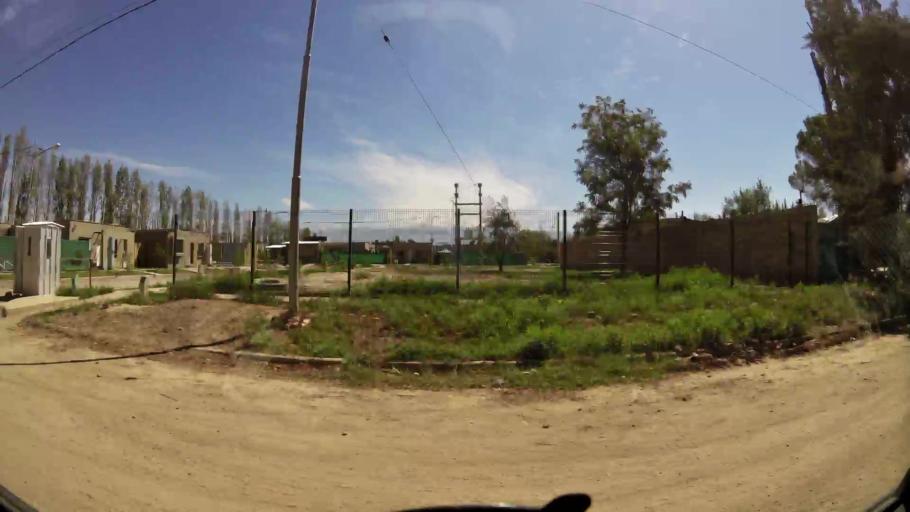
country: AR
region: Mendoza
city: Lujan de Cuyo
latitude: -32.9856
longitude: -68.8506
